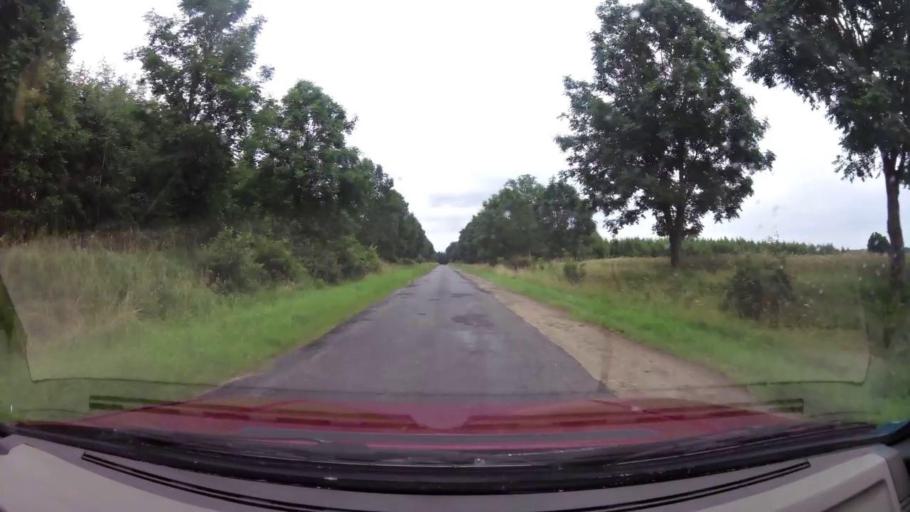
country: PL
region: West Pomeranian Voivodeship
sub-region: Powiat swidwinski
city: Rabino
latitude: 53.9377
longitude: 15.9596
